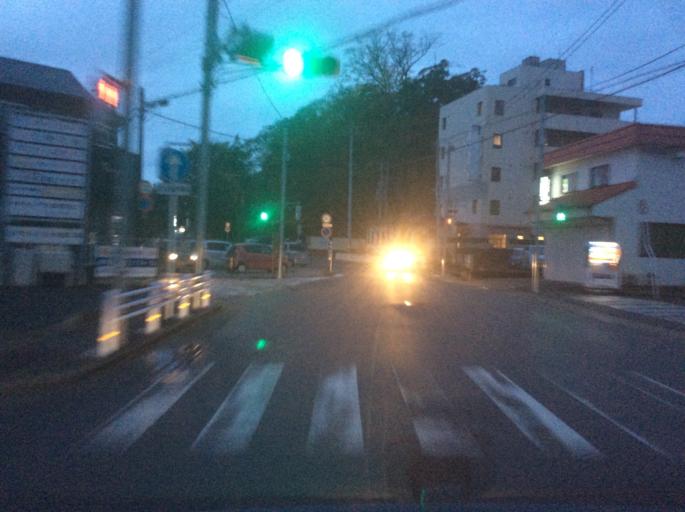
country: JP
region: Fukushima
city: Iwaki
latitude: 37.0624
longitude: 140.8940
